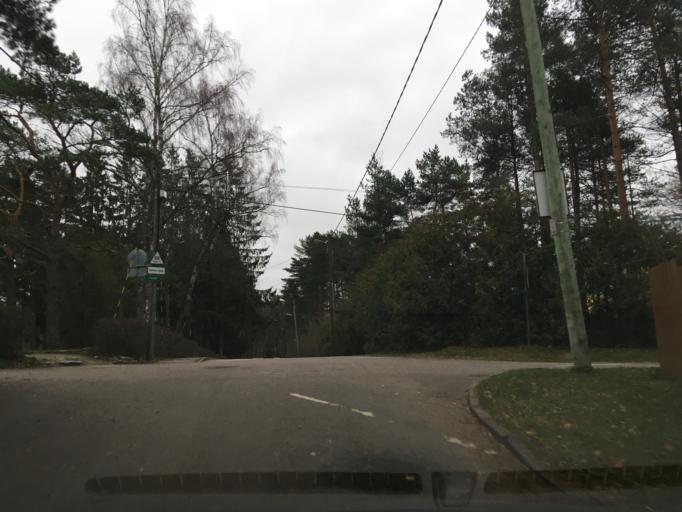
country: EE
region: Harju
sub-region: Saue vald
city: Laagri
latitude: 59.3807
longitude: 24.6886
